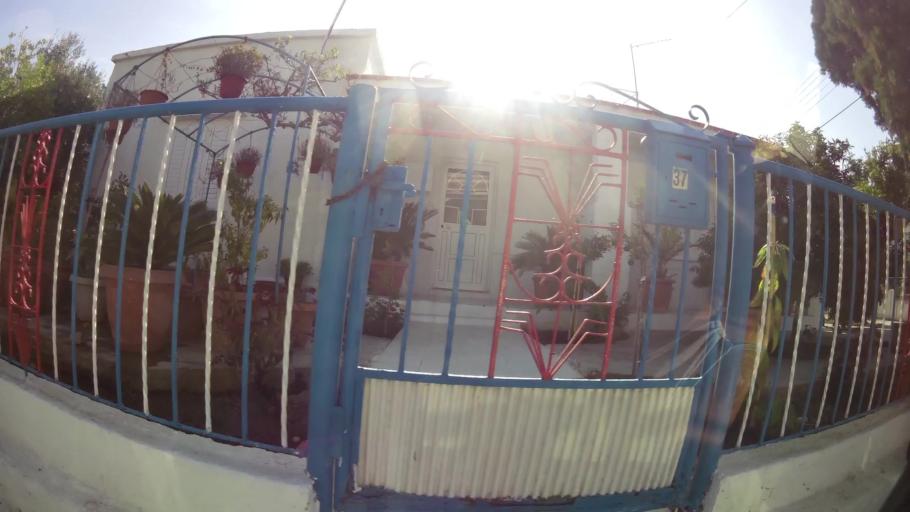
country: CY
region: Larnaka
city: Aradippou
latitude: 34.9506
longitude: 33.5889
